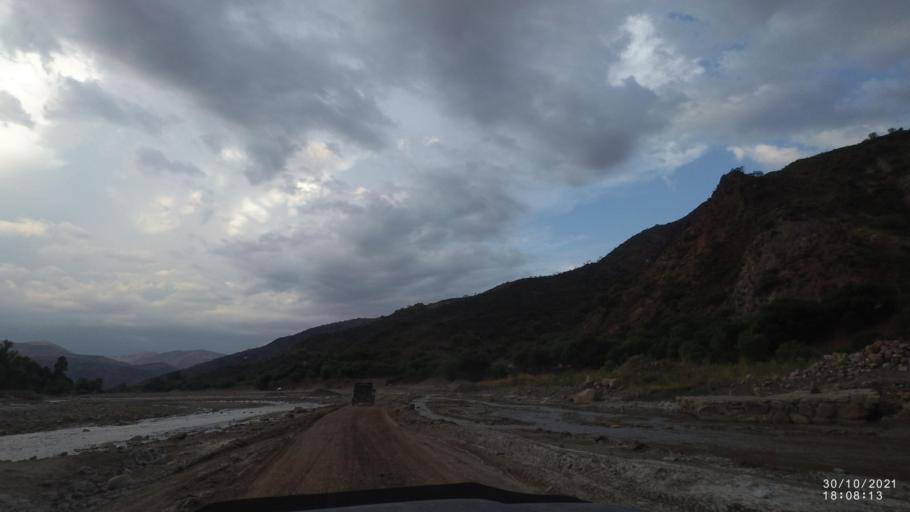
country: BO
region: Cochabamba
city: Sipe Sipe
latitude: -17.5609
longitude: -66.4485
